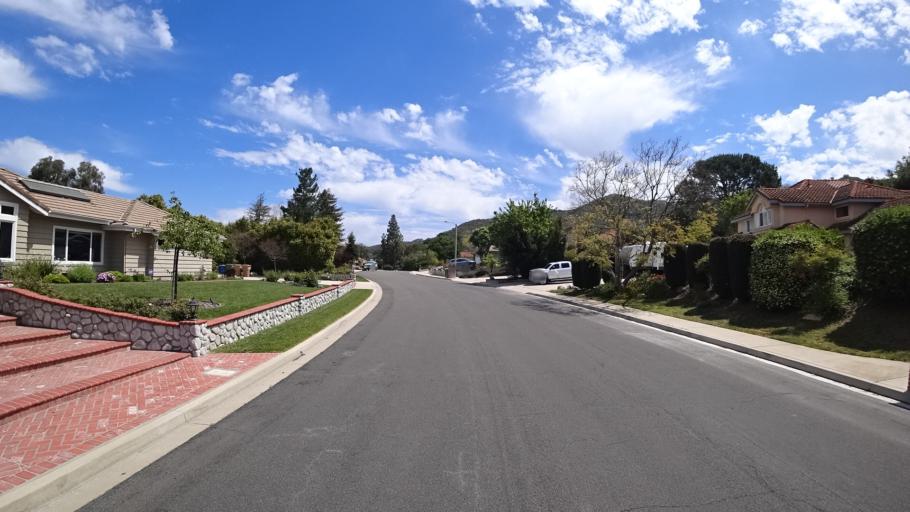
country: US
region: California
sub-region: Ventura County
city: Casa Conejo
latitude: 34.1600
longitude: -118.9422
